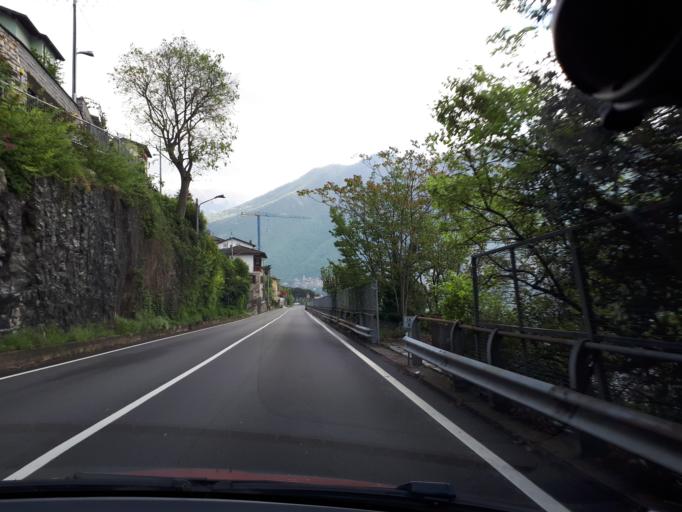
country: IT
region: Lombardy
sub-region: Provincia di Como
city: Carate Urio
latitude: 45.8741
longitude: 9.1256
